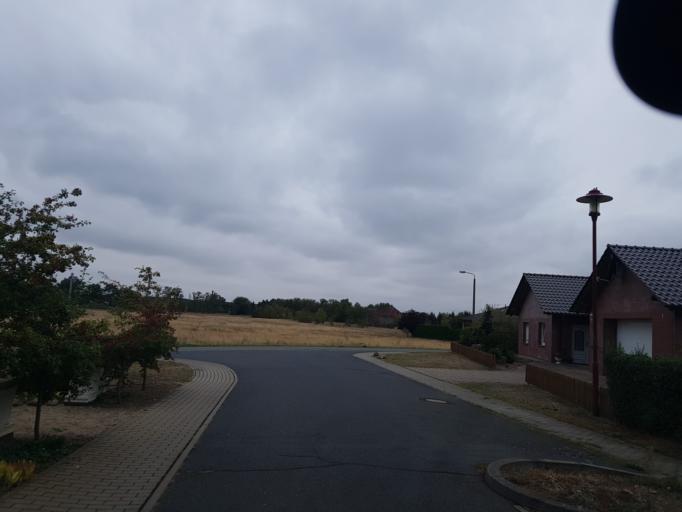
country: DE
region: Saxony-Anhalt
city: Jessen
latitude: 51.7907
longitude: 12.9718
